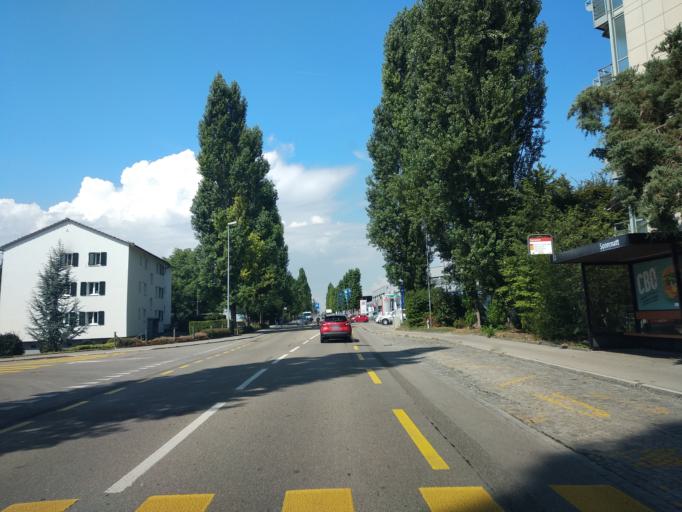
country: CH
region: Thurgau
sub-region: Frauenfeld District
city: Frauenfeld
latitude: 47.5623
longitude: 8.8824
